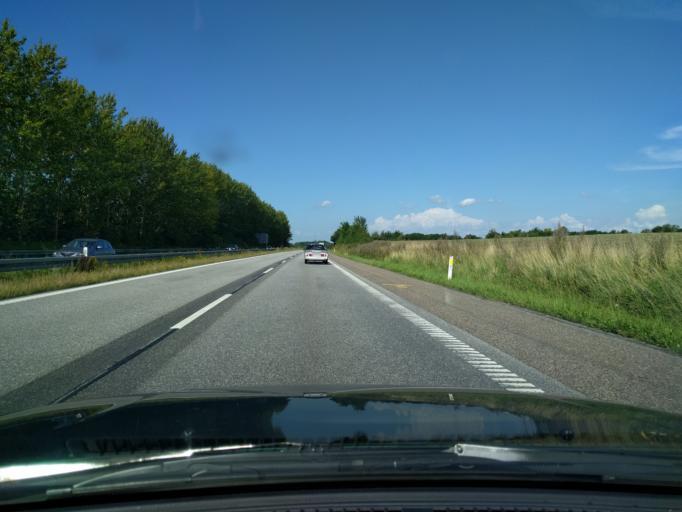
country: DK
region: Zealand
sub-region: Vordingborg Kommune
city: Orslev
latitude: 55.0641
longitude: 11.9673
